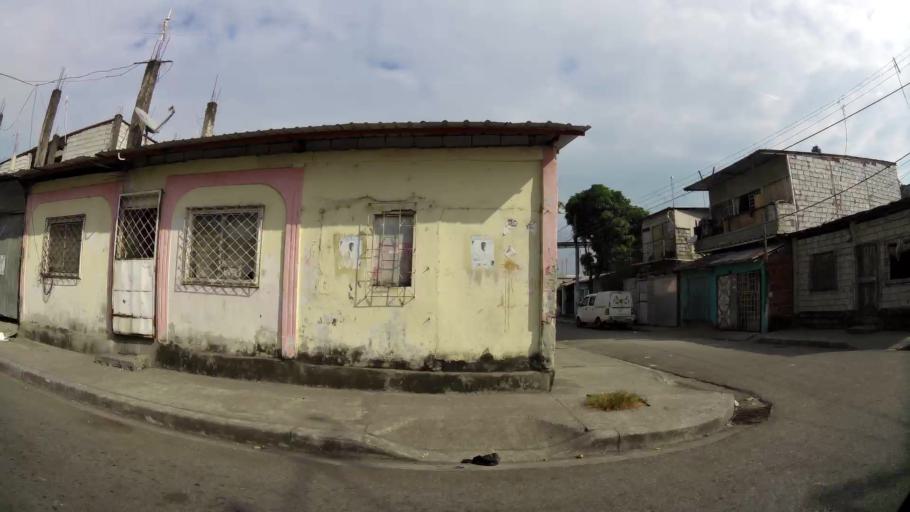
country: EC
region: Guayas
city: Guayaquil
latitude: -2.2492
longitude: -79.9122
